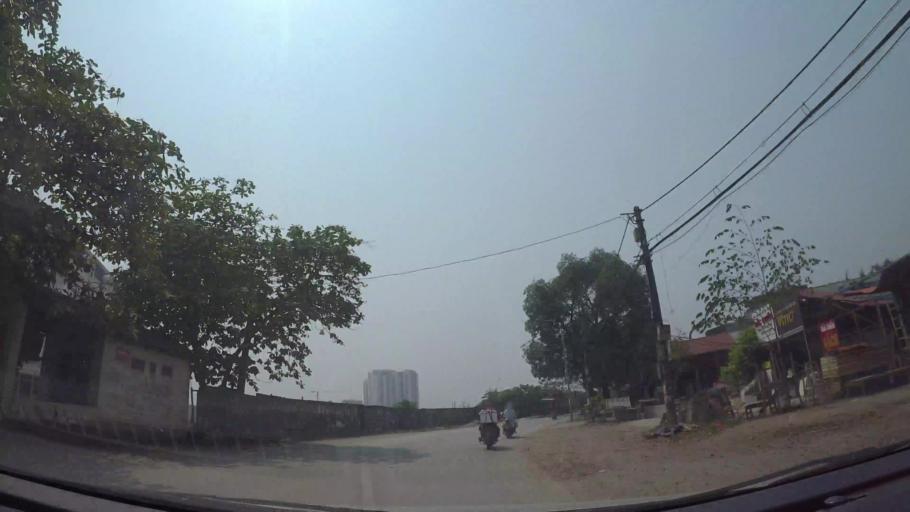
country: VN
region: Ha Noi
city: Ha Dong
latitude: 20.9893
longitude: 105.7648
